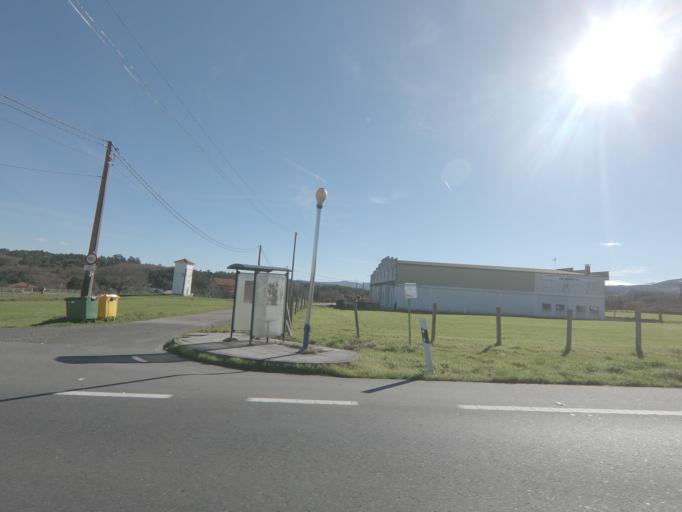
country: ES
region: Galicia
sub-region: Provincia de Pontevedra
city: Silleda
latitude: 42.6866
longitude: -8.2098
